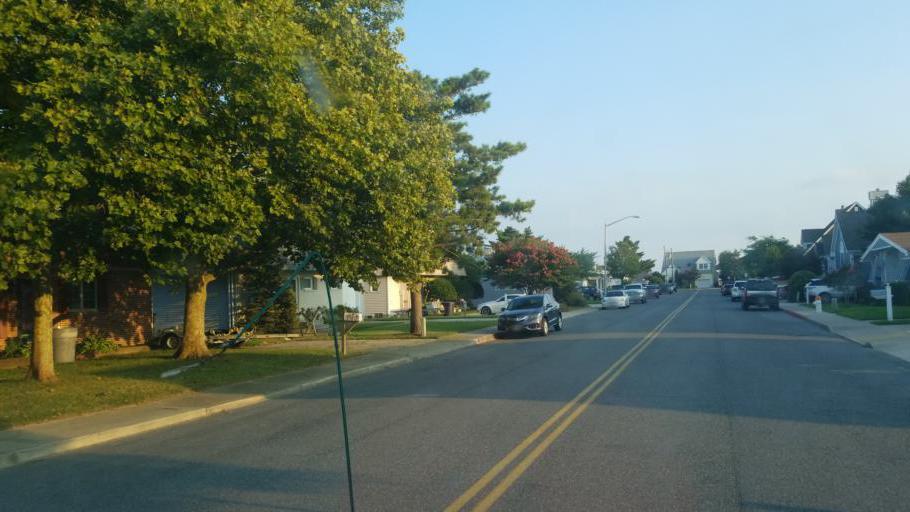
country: US
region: Maryland
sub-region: Worcester County
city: Ocean City
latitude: 38.4183
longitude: -75.0651
